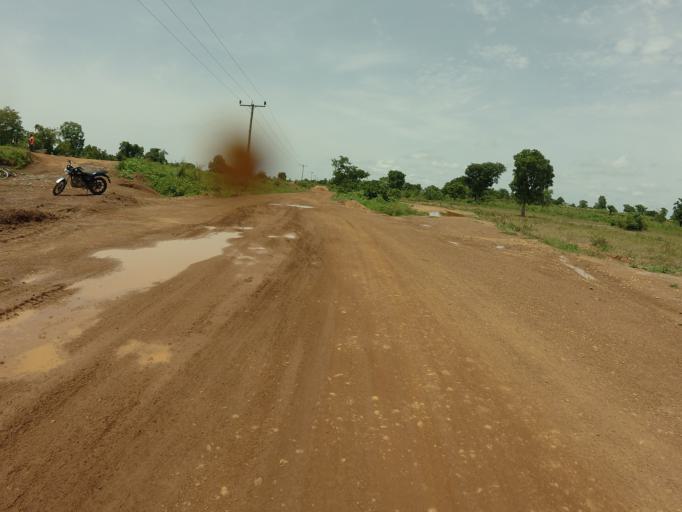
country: GH
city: Kpandae
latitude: 8.7145
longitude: 0.1453
